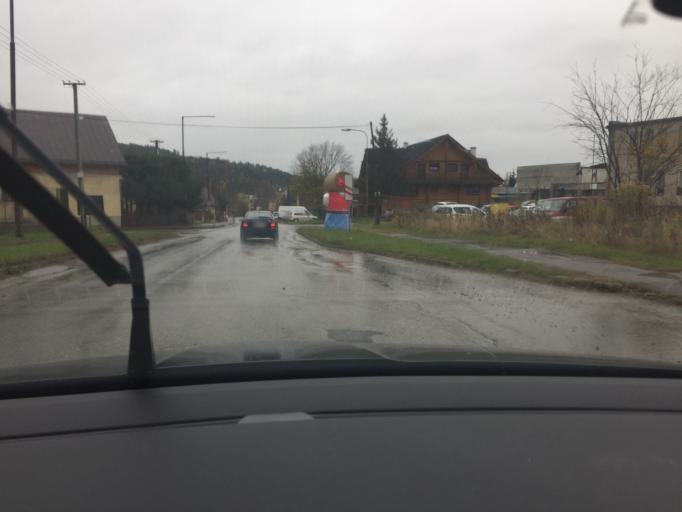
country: SK
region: Presovsky
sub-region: Okres Presov
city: Kezmarok
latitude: 49.1512
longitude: 20.4279
